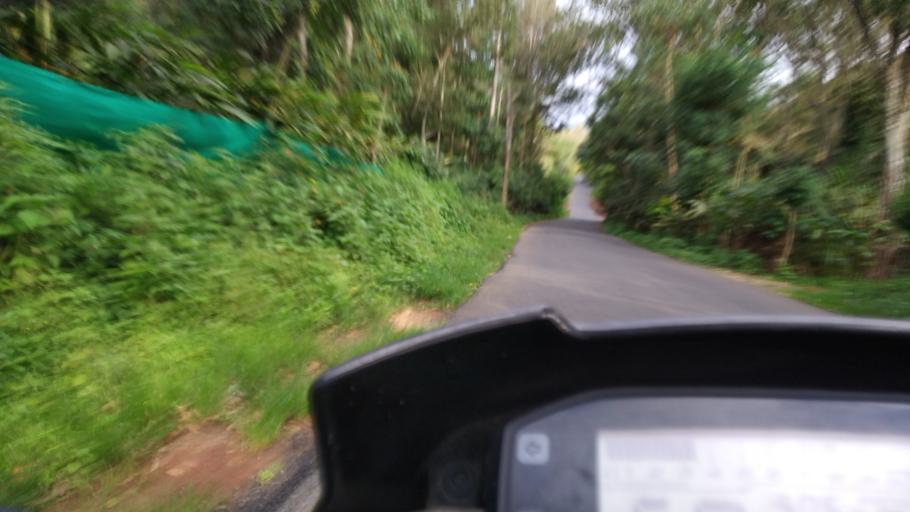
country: IN
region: Tamil Nadu
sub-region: Theni
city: Bodinayakkanur
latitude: 10.0356
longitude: 77.2228
